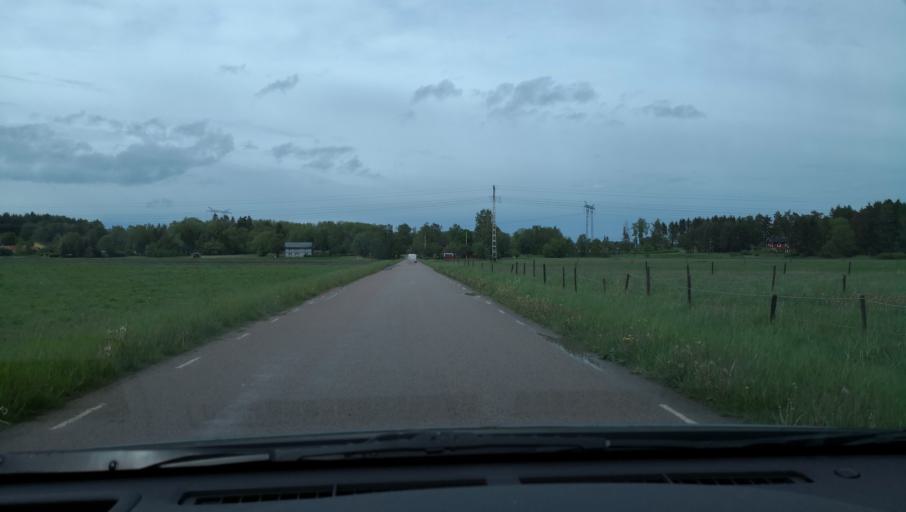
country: SE
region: Uppsala
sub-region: Enkopings Kommun
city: Orsundsbro
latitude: 59.6850
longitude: 17.3794
